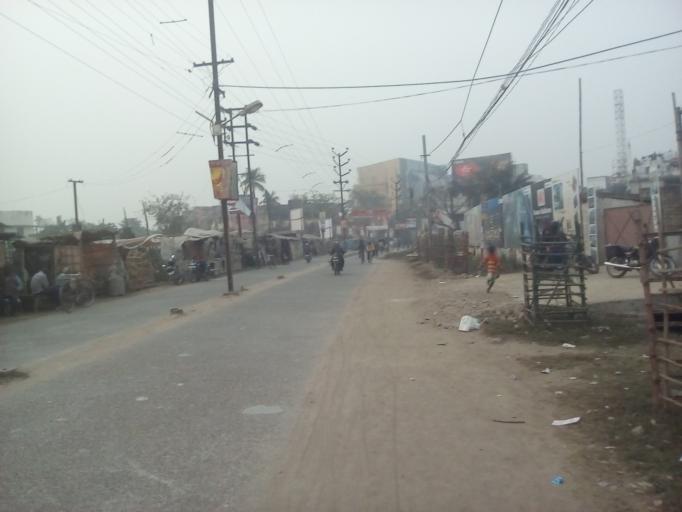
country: IN
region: Bihar
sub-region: Muzaffarpur
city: Muzaffarpur
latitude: 26.1079
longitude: 85.3967
